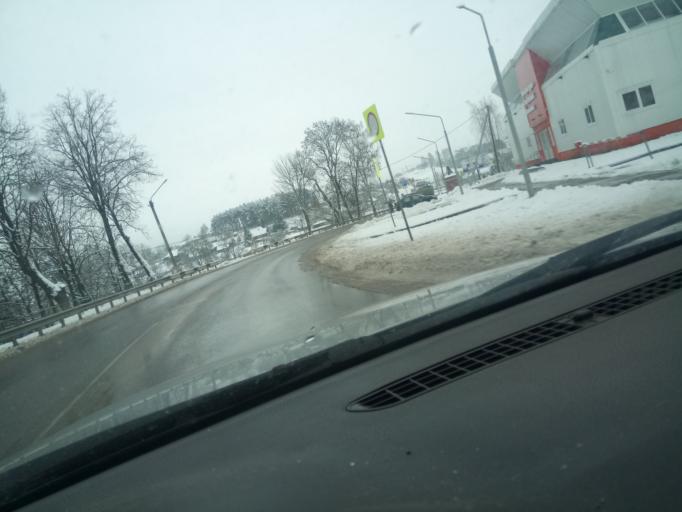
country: BY
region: Vitebsk
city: Syanno
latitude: 54.8148
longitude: 29.7133
